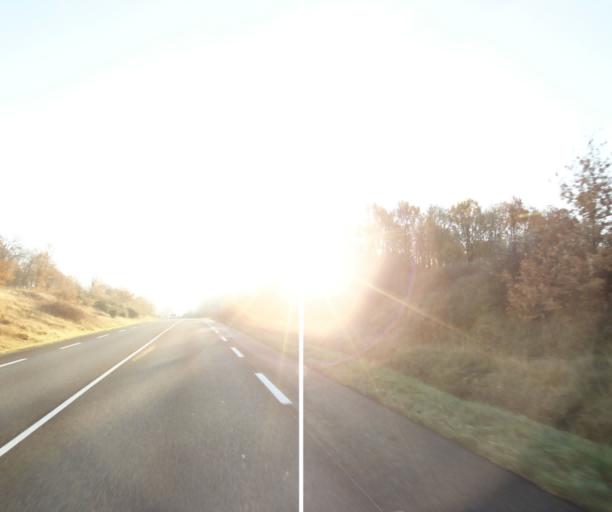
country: FR
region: Poitou-Charentes
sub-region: Departement de la Charente-Maritime
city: Chaniers
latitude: 45.7284
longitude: -0.5250
